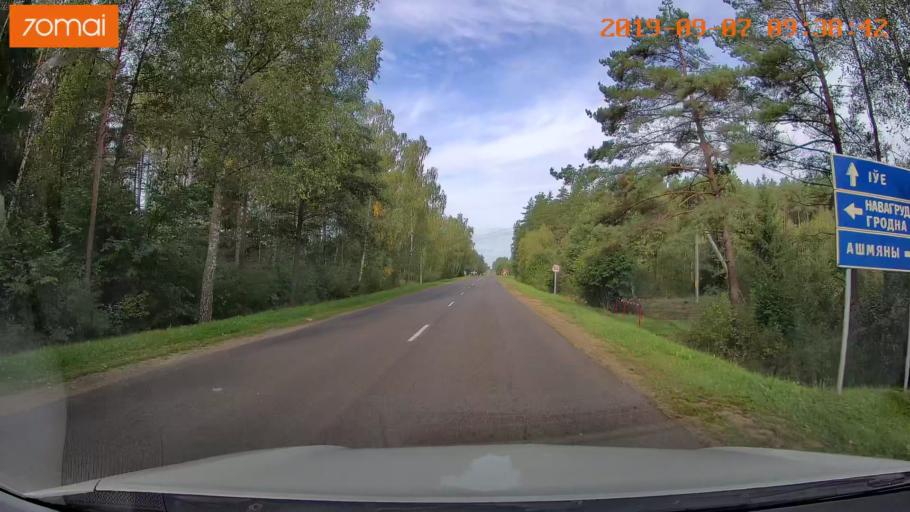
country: BY
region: Grodnenskaya
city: Iwye
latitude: 53.9251
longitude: 25.8155
